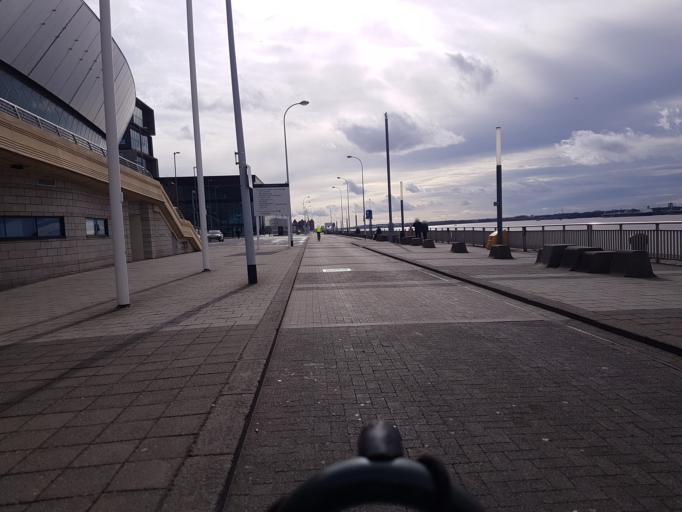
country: GB
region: England
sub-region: Liverpool
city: Liverpool
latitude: 53.3970
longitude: -2.9920
